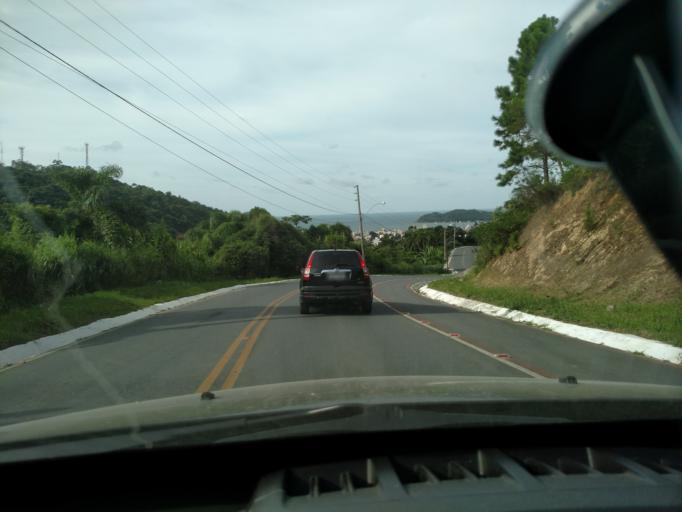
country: BR
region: Santa Catarina
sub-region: Porto Belo
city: Porto Belo
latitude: -27.1611
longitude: -48.4936
